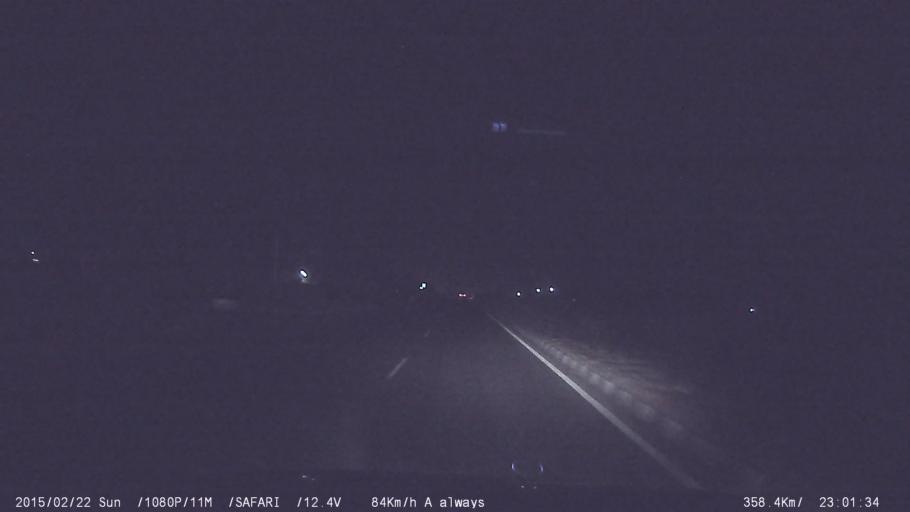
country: IN
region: Tamil Nadu
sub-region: Namakkal
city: Rasipuram
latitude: 11.3650
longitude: 78.1644
